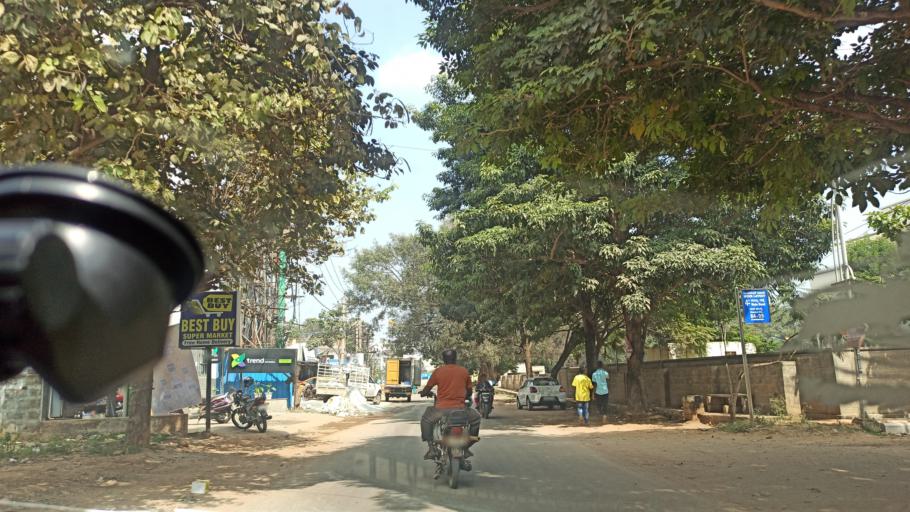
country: IN
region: Karnataka
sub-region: Bangalore Urban
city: Yelahanka
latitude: 13.0746
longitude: 77.6045
